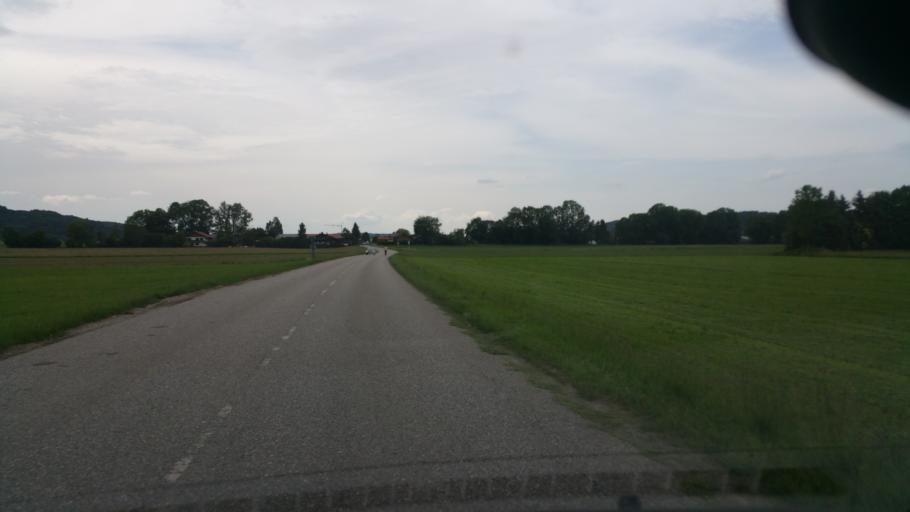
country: DE
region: Bavaria
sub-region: Upper Bavaria
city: Bruckmuhl
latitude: 47.8667
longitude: 11.9211
